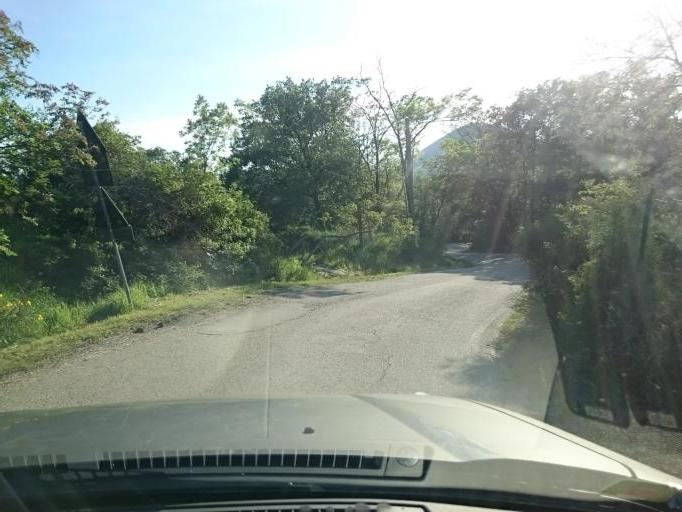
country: IT
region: Veneto
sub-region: Provincia di Padova
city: Arqua Petrarca
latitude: 45.2869
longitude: 11.7042
